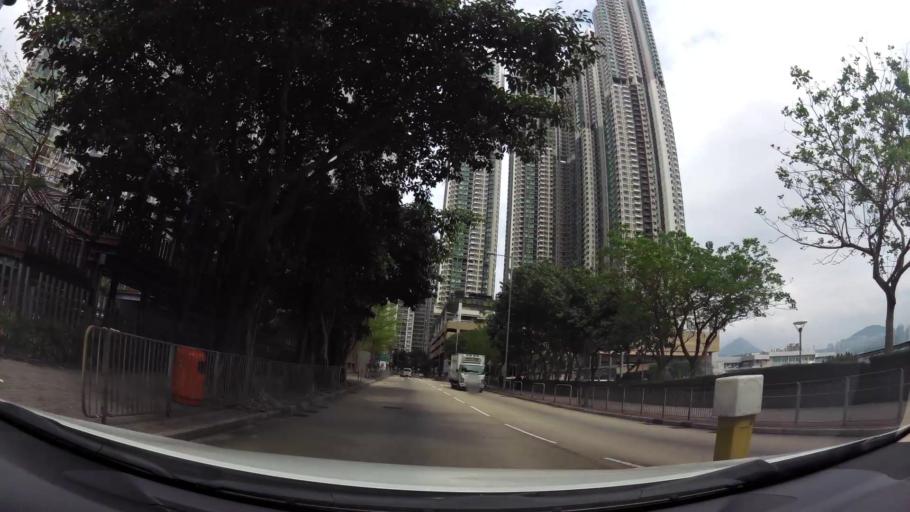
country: HK
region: Wanchai
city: Wan Chai
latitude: 22.2834
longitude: 114.2255
